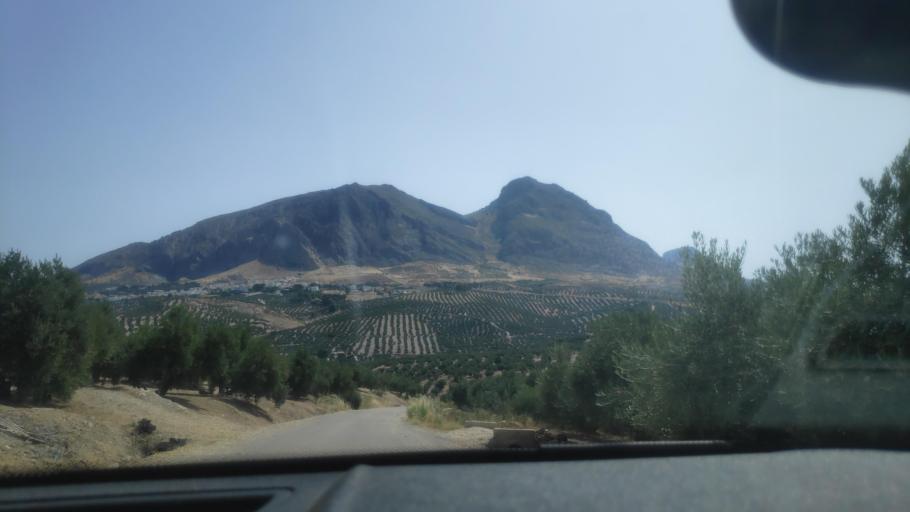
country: ES
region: Andalusia
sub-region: Provincia de Jaen
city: Jimena
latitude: 37.8080
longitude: -3.4330
